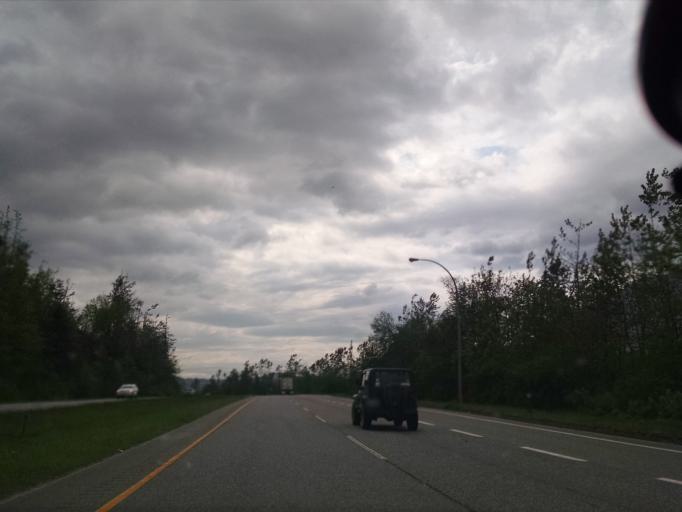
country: CA
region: British Columbia
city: Agassiz
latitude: 49.2926
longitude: -121.6626
